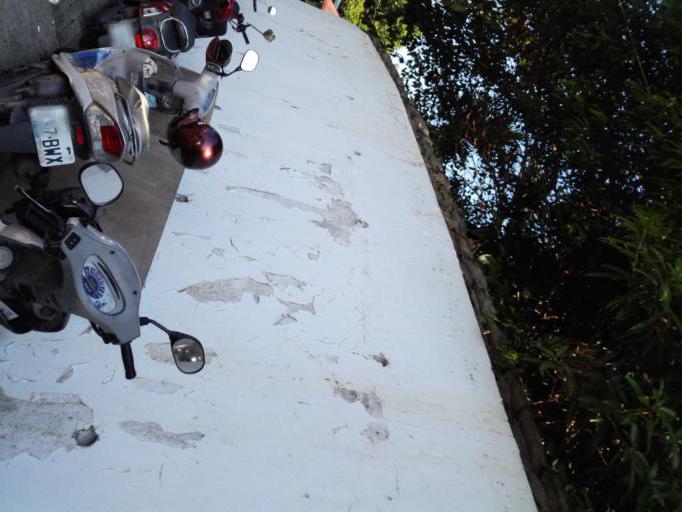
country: TW
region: Taiwan
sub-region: Taichung City
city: Taichung
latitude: 24.1788
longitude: 120.7334
